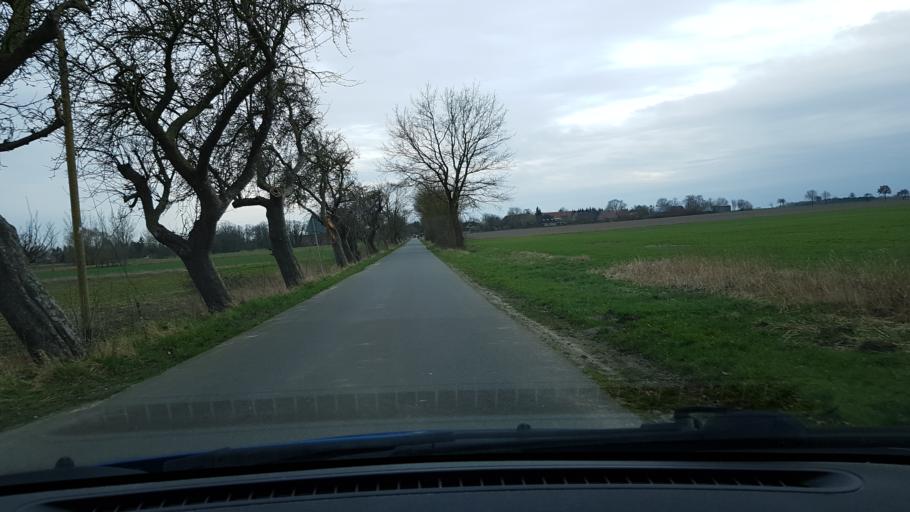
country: DE
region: Lower Saxony
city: Oetzen
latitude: 53.0050
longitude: 10.6538
